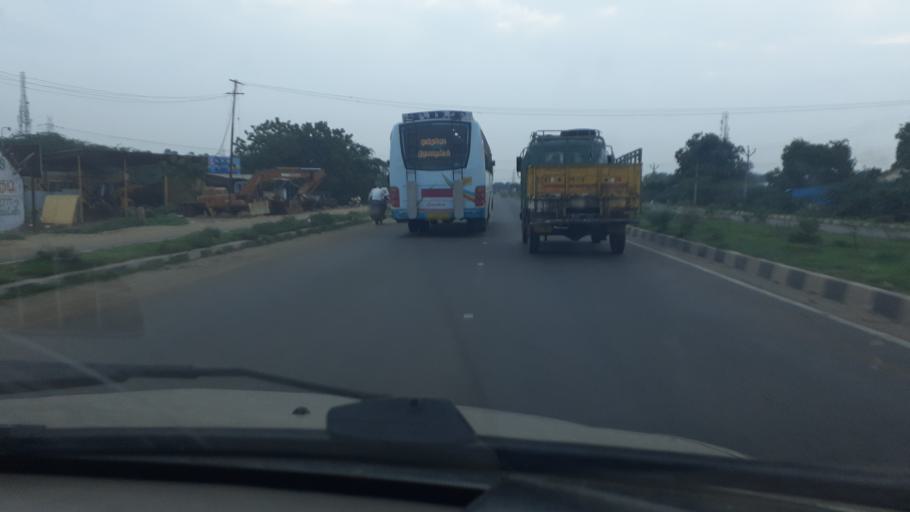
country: IN
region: Tamil Nadu
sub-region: Thoothukkudi
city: Korampallam
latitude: 8.7760
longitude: 78.0891
